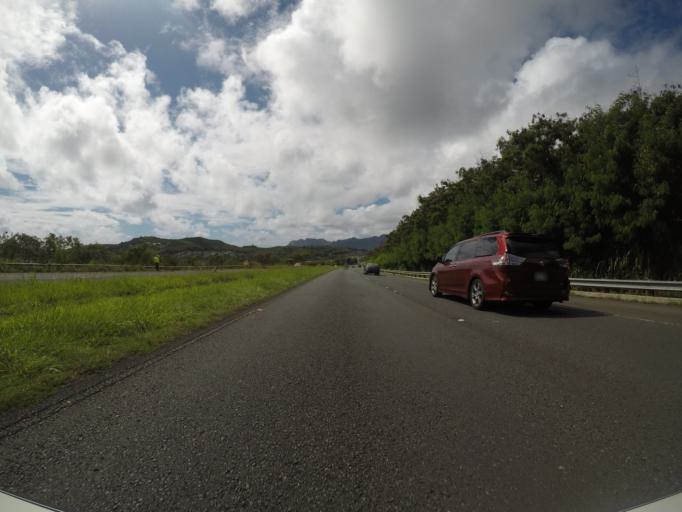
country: US
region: Hawaii
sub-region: Honolulu County
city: Maunawili
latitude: 21.3720
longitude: -157.7434
